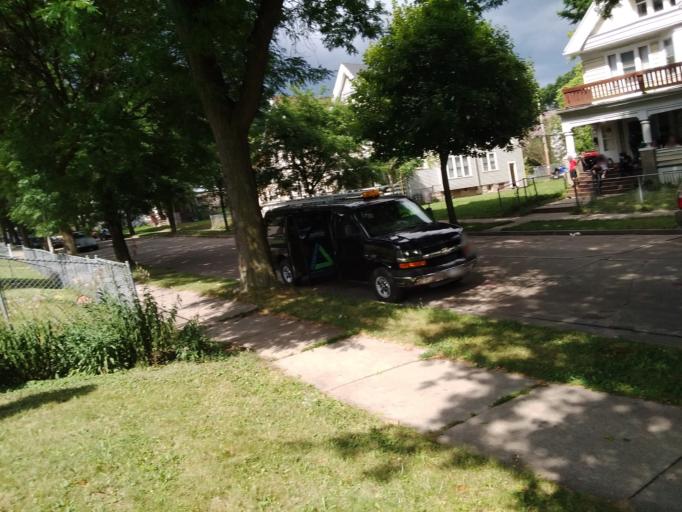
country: US
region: Wisconsin
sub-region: Milwaukee County
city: Wauwatosa
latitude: 43.0612
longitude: -87.9702
